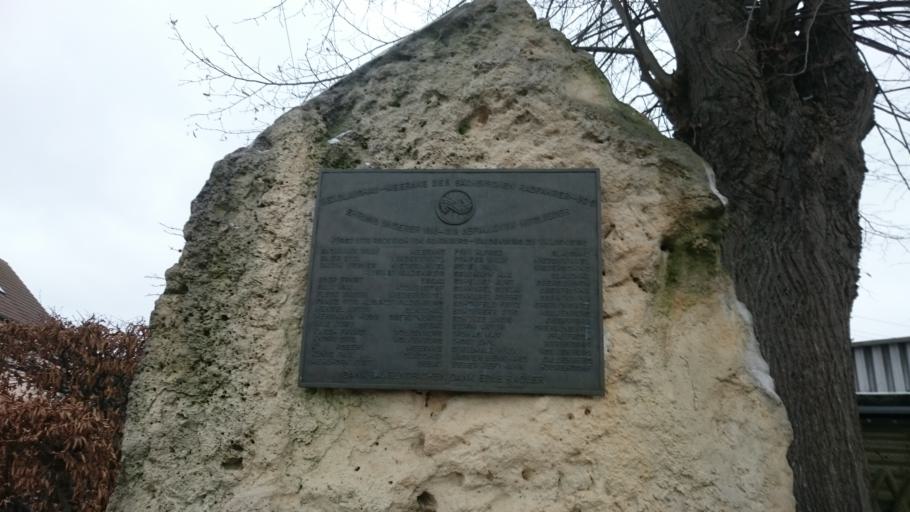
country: DE
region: Saxony
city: Pfaffroda
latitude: 50.8341
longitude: 12.5020
